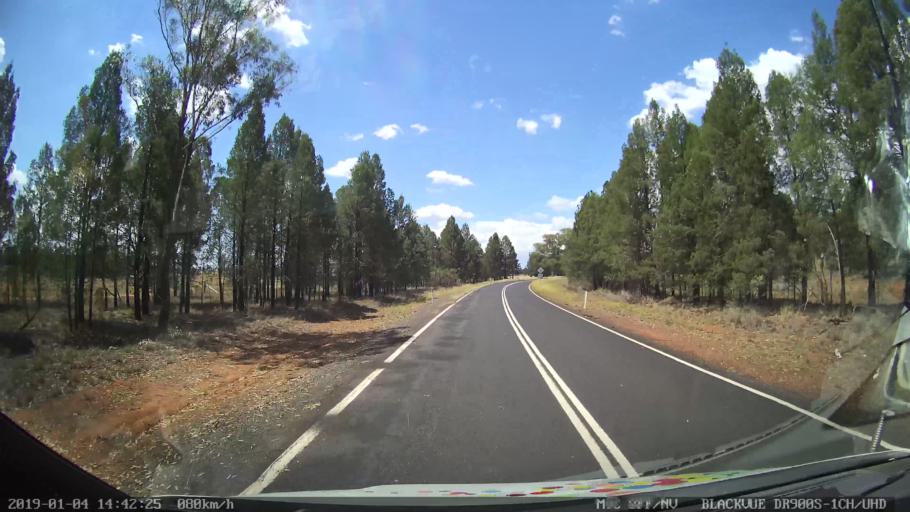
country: AU
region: New South Wales
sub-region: Dubbo Municipality
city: Dubbo
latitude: -32.1282
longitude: 148.6417
